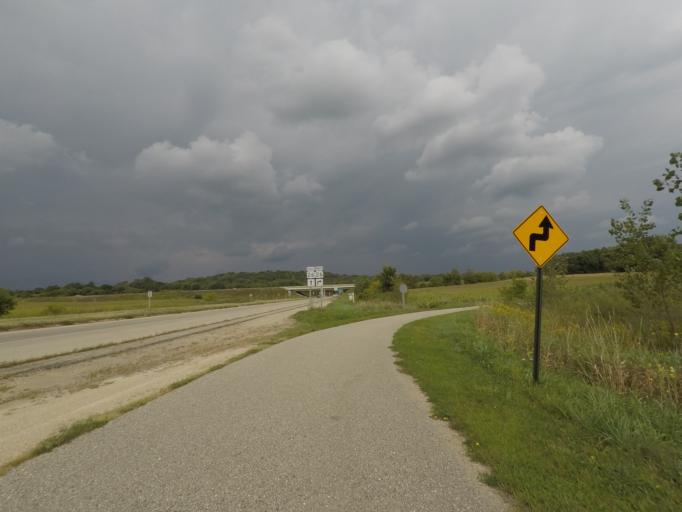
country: US
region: Wisconsin
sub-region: Jefferson County
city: Fort Atkinson
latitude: 42.9516
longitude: -88.8291
